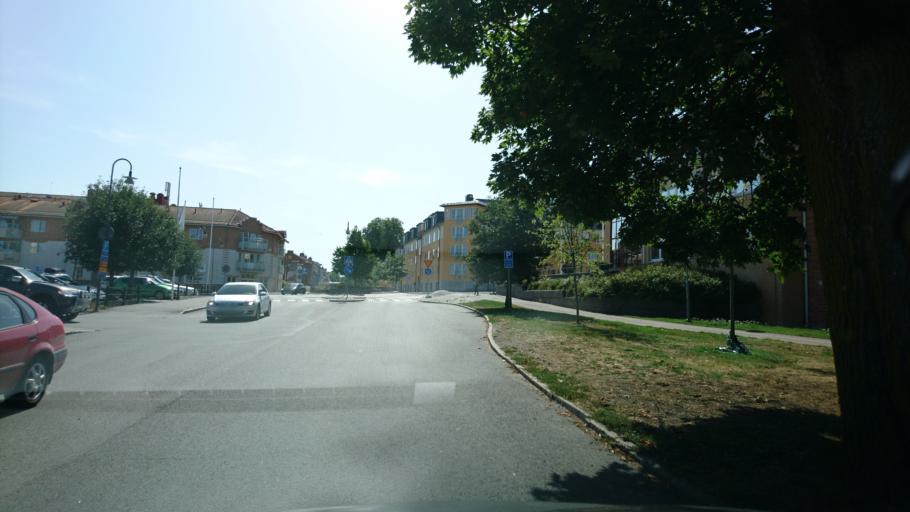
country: SE
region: Soedermanland
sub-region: Strangnas Kommun
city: Strangnas
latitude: 59.3764
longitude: 17.0245
